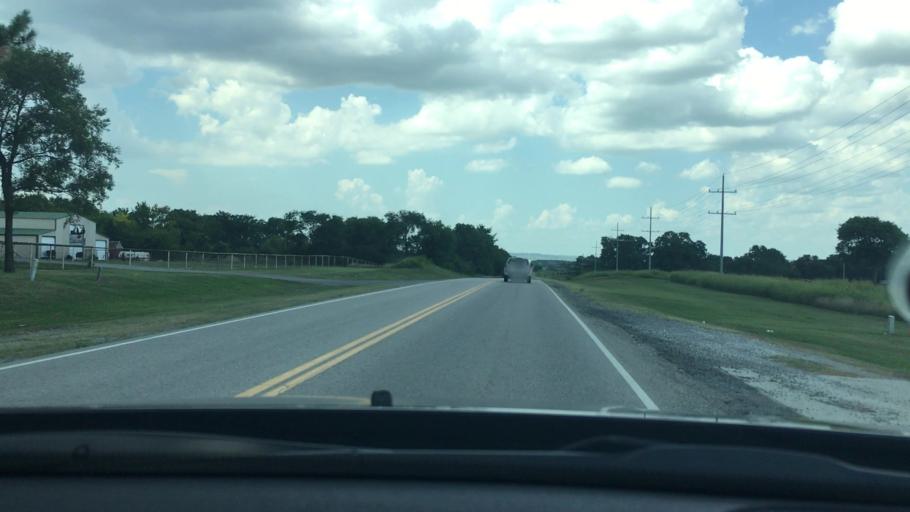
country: US
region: Oklahoma
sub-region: Pontotoc County
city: Ada
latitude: 34.6723
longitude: -96.6349
